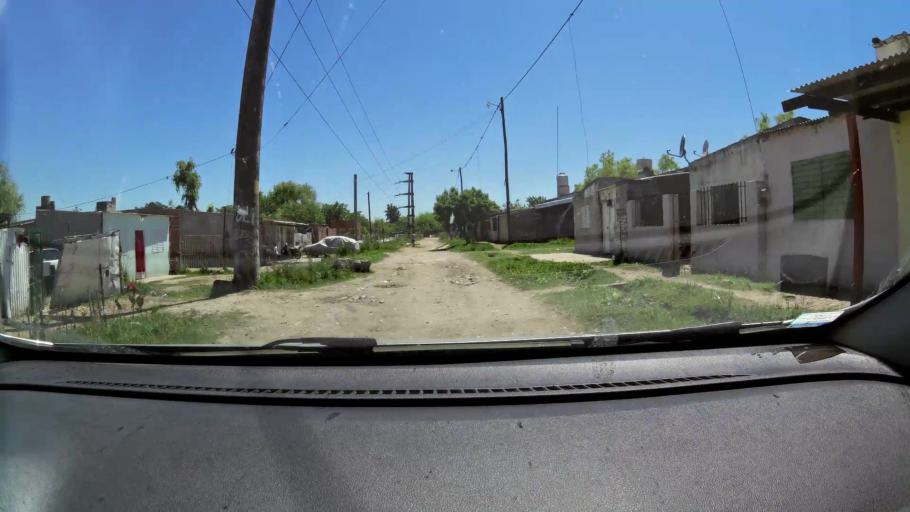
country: AR
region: Santa Fe
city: Santa Fe de la Vera Cruz
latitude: -31.6142
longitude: -60.7204
